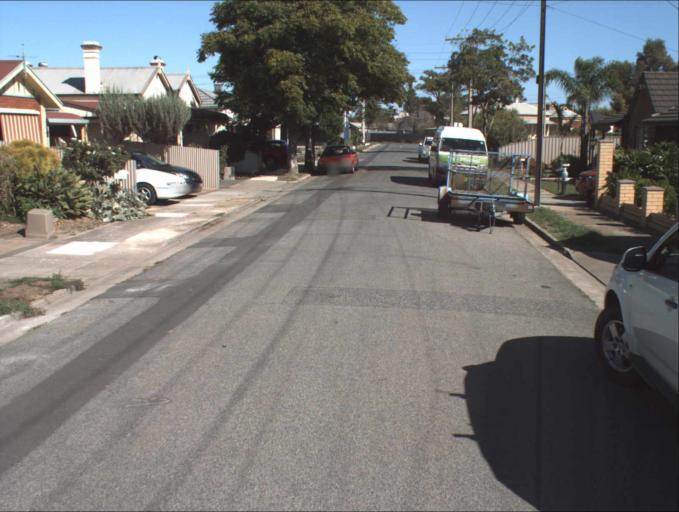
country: AU
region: South Australia
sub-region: Port Adelaide Enfield
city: Alberton
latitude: -34.8571
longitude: 138.5218
